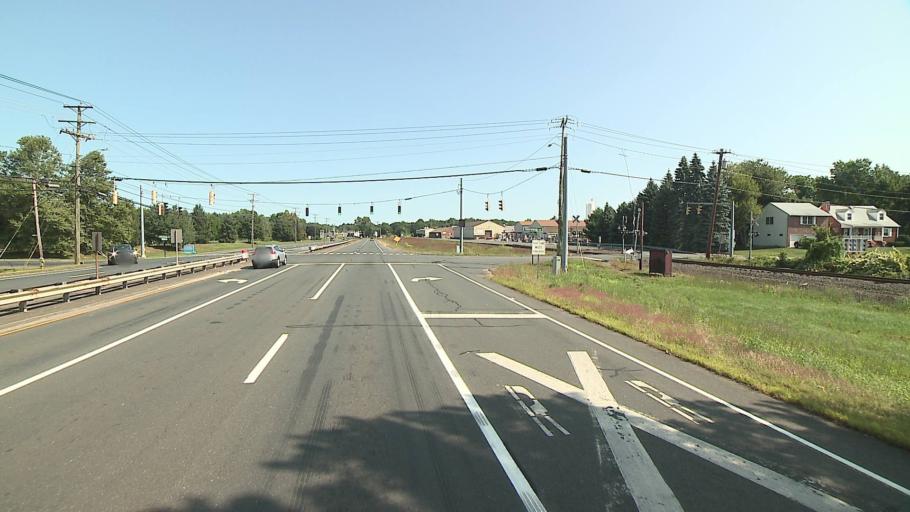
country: US
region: Connecticut
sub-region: Hartford County
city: South Windsor
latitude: 41.8417
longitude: -72.6009
